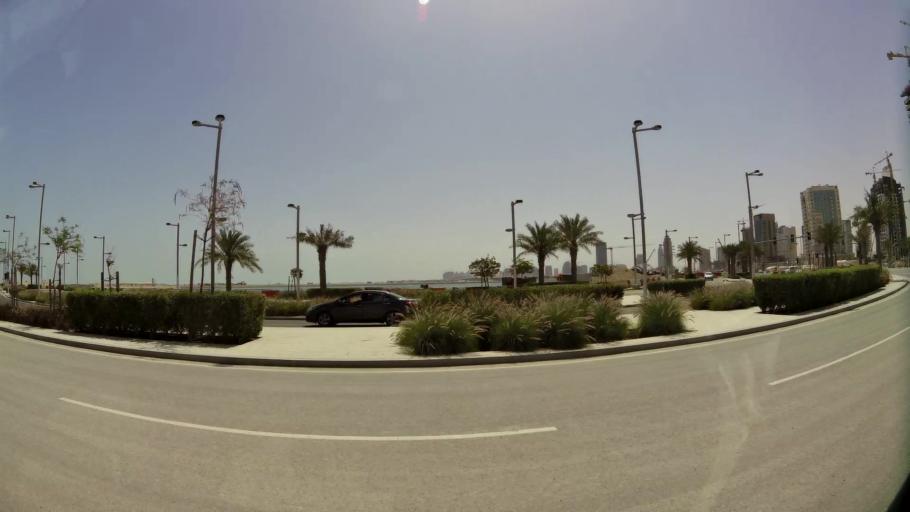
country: QA
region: Baladiyat Umm Salal
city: Umm Salal Muhammad
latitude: 25.4004
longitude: 51.5219
